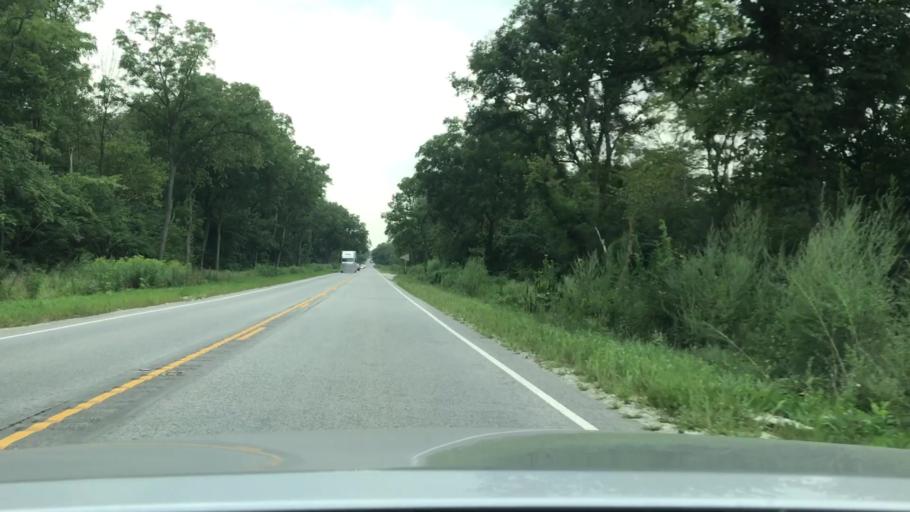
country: US
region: Illinois
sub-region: DuPage County
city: Burr Ridge
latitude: 41.6878
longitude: -87.9016
